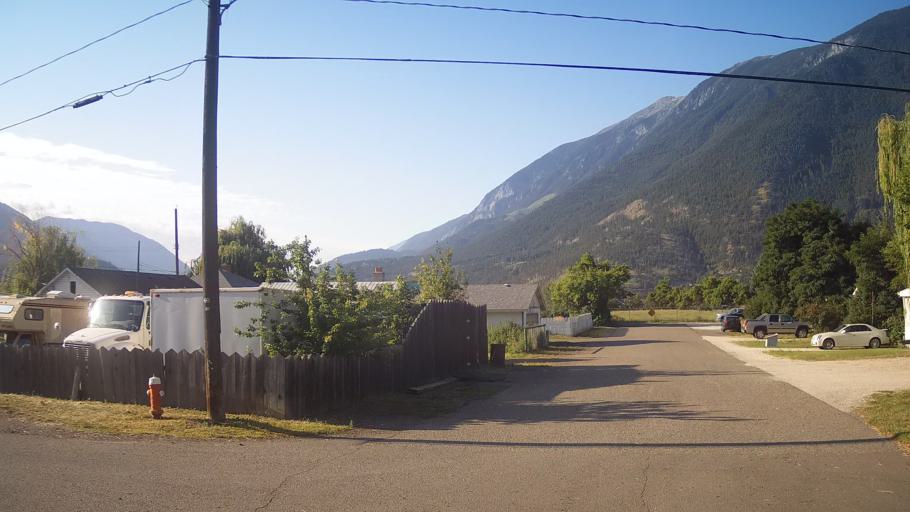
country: CA
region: British Columbia
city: Lillooet
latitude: 50.6868
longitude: -121.9383
